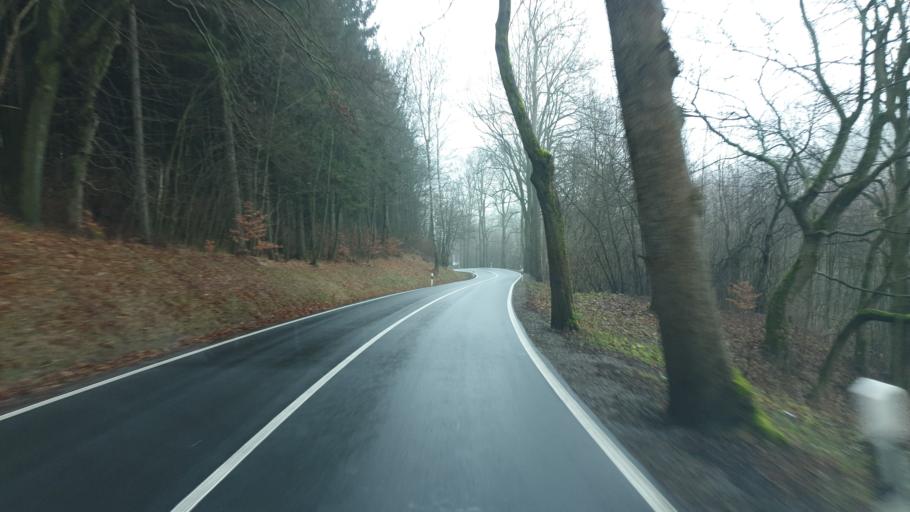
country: DE
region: Saxony
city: Neuhausen
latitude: 50.6839
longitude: 13.4603
